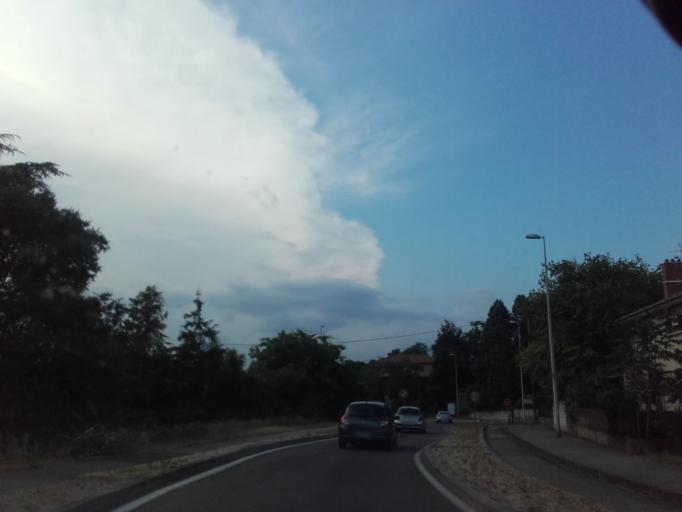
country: FR
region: Rhone-Alpes
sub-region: Departement de l'Isere
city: Le Peage-de-Roussillon
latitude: 45.3767
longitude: 4.7990
